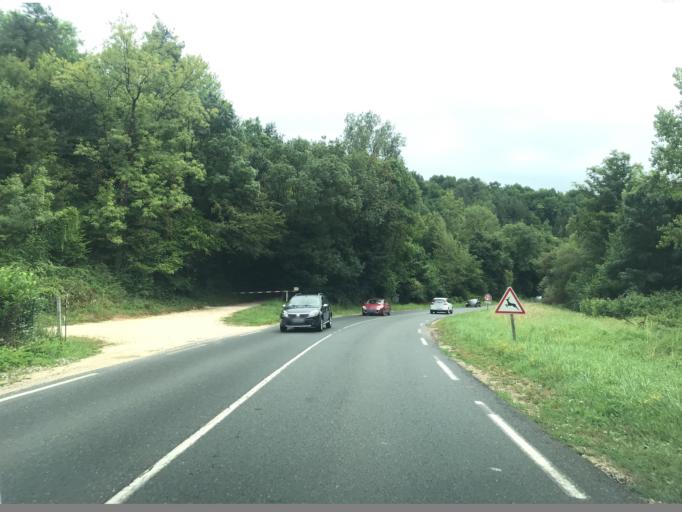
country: FR
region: Aquitaine
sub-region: Departement de la Dordogne
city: Chancelade
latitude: 45.2148
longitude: 0.6717
